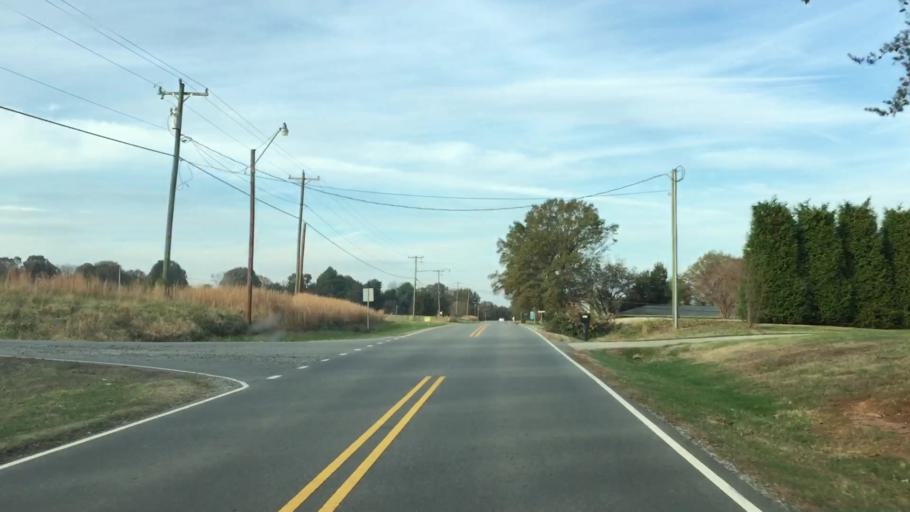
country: US
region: North Carolina
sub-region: Rockingham County
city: Reidsville
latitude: 36.3432
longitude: -79.6995
